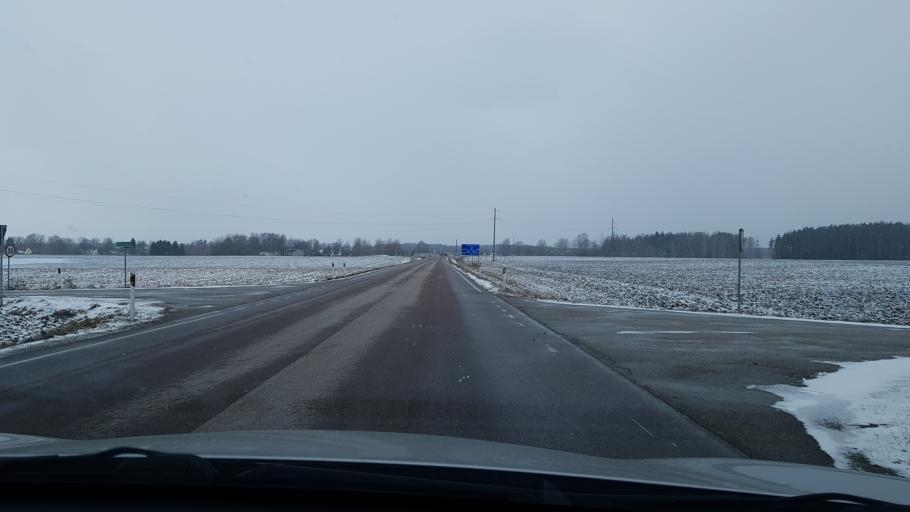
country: EE
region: Polvamaa
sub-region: Polva linn
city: Polva
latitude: 58.0896
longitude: 27.1026
